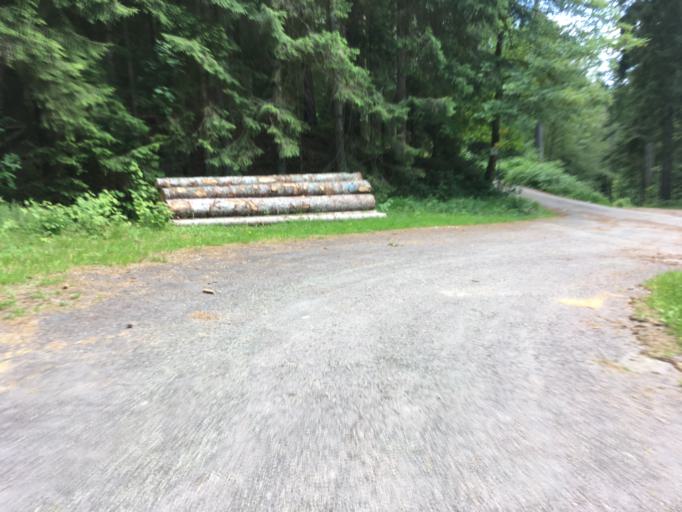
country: DE
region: Baden-Wuerttemberg
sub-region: Karlsruhe Region
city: Baiersbronn
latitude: 48.5633
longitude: 8.4200
